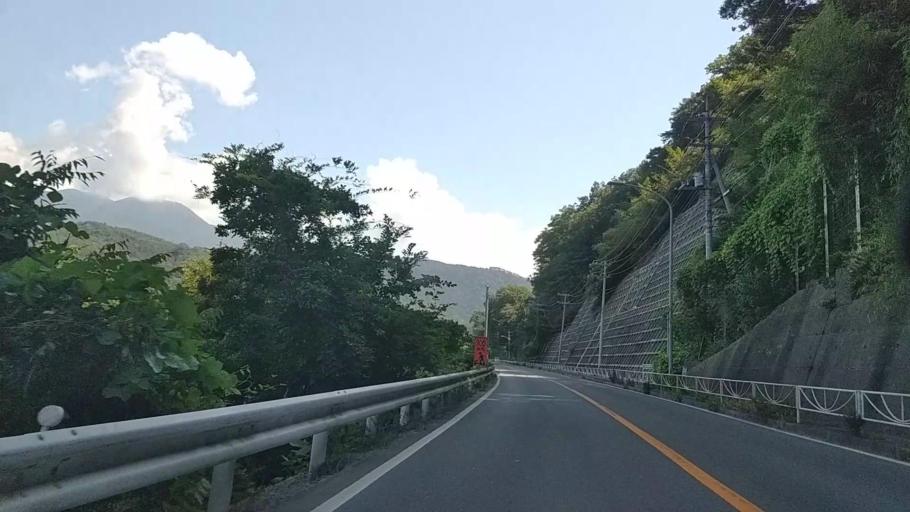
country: JP
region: Yamanashi
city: Ryuo
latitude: 35.4600
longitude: 138.4420
